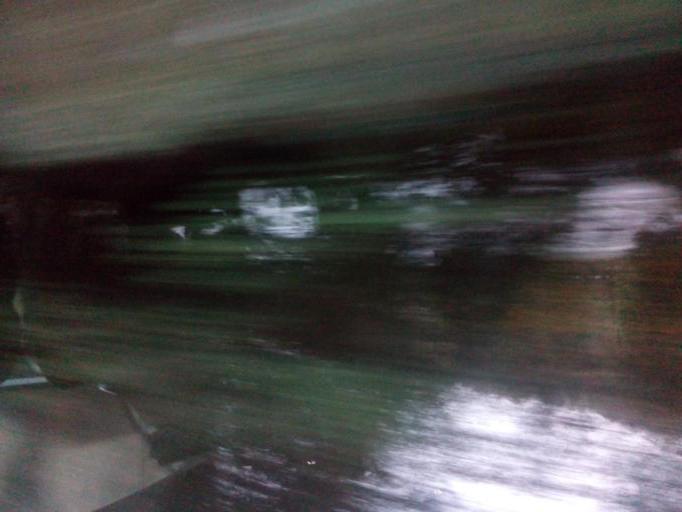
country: GB
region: England
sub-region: Cornwall
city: Liskeard
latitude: 50.4553
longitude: -4.5641
